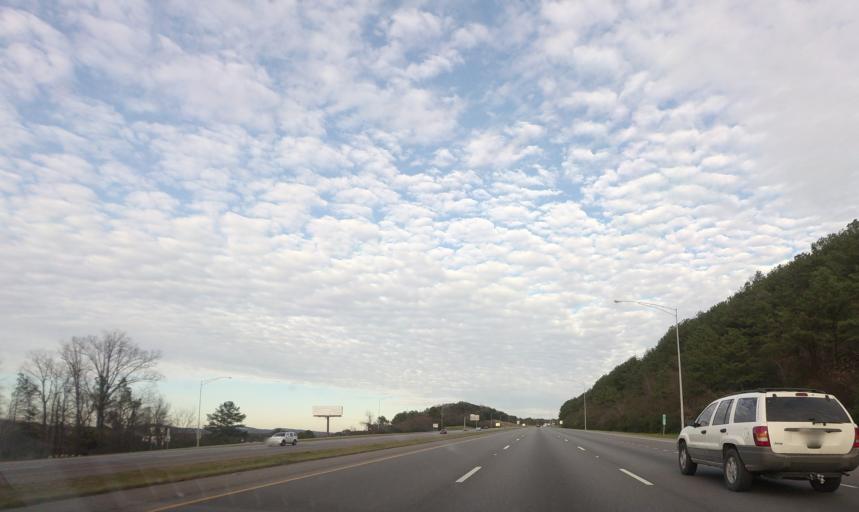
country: US
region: Alabama
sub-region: Jefferson County
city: Irondale
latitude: 33.5366
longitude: -86.6931
